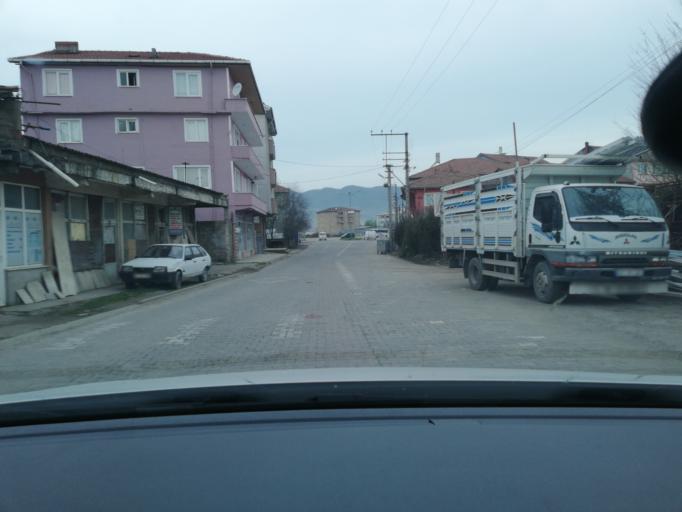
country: TR
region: Zonguldak
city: Caycuma
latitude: 41.4162
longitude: 32.0950
